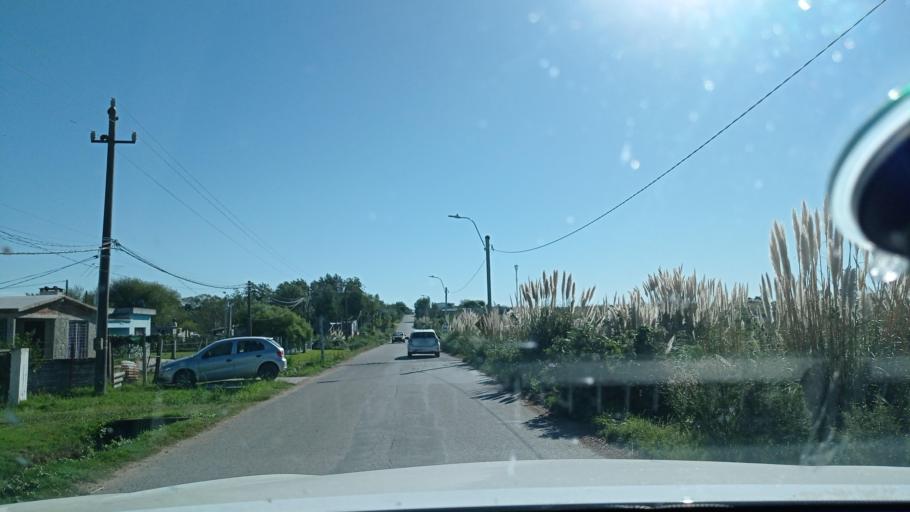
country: UY
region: Canelones
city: Joaquin Suarez
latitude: -34.7570
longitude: -55.9876
